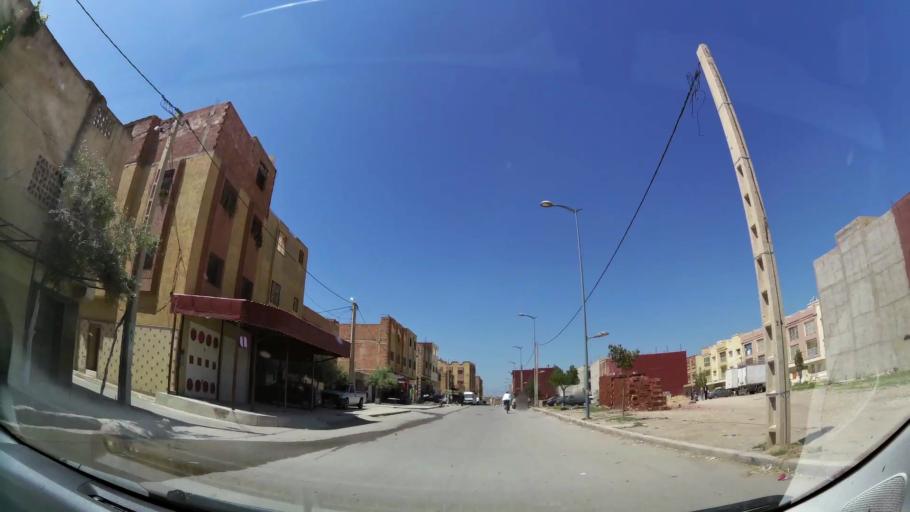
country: MA
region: Oriental
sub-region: Oujda-Angad
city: Oujda
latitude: 34.6816
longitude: -1.9510
